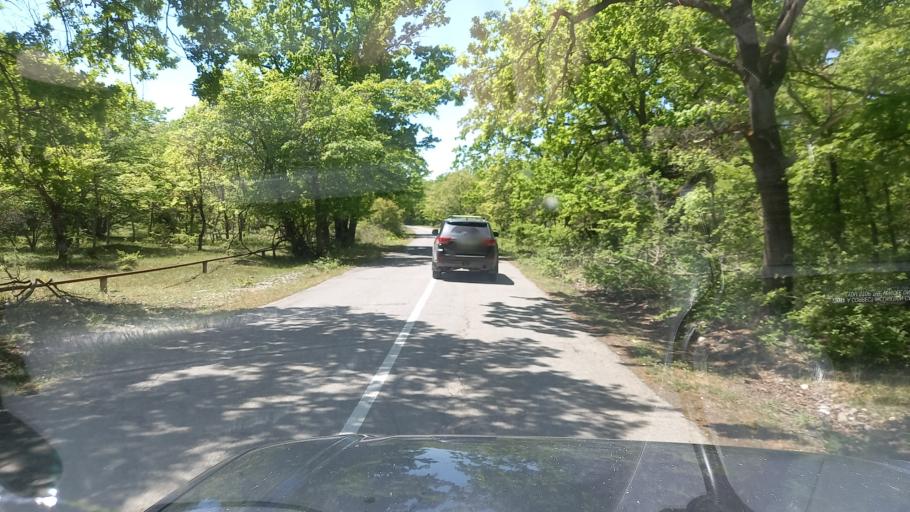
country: RU
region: Dagestan
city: Samur
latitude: 41.8398
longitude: 48.5704
